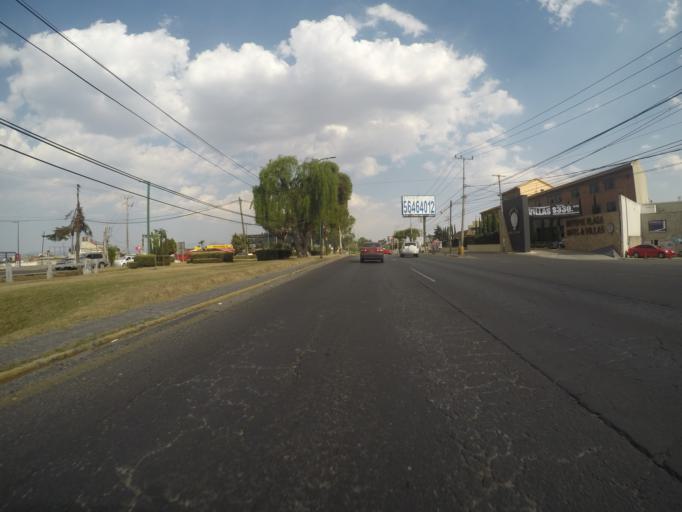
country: MX
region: Mexico
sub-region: Metepec
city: San Jorge Pueblo Nuevo
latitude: 19.2520
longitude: -99.6158
